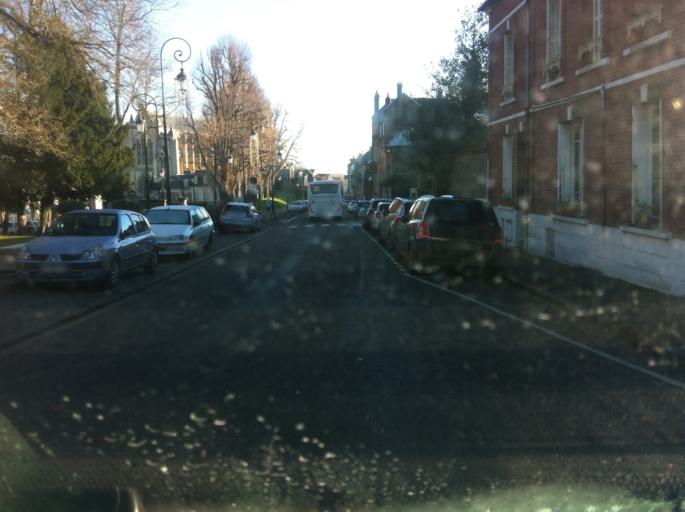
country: FR
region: Haute-Normandie
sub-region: Departement de la Seine-Maritime
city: Eu
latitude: 50.0485
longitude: 1.4160
